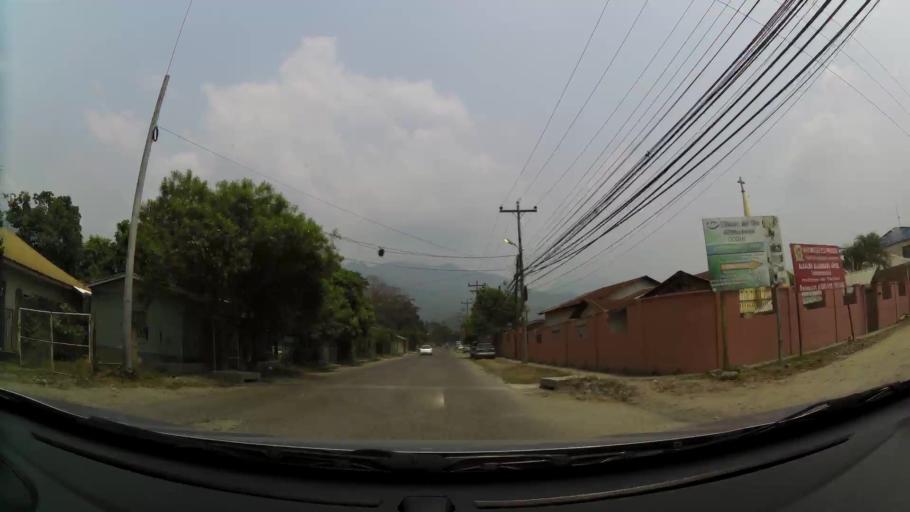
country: HN
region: Yoro
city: El Progreso
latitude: 15.3960
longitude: -87.7974
